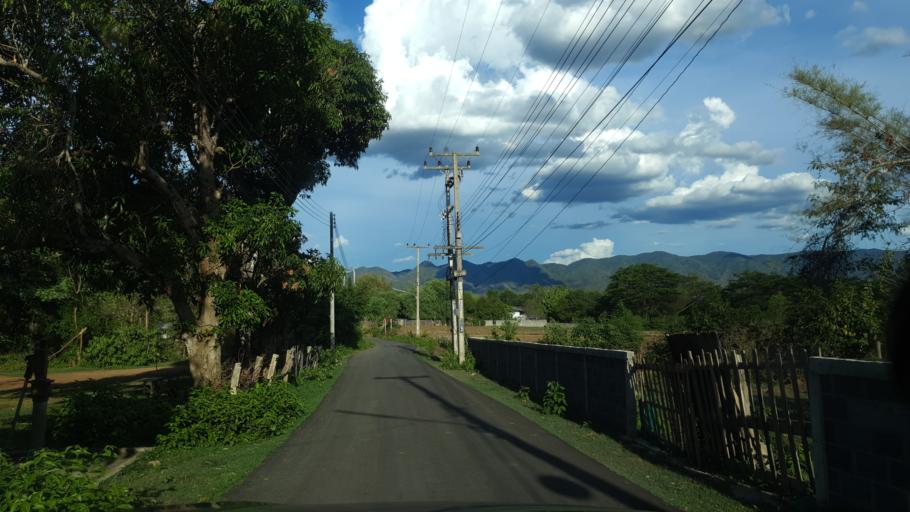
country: TH
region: Lampang
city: Sop Prap
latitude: 17.8762
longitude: 99.2984
